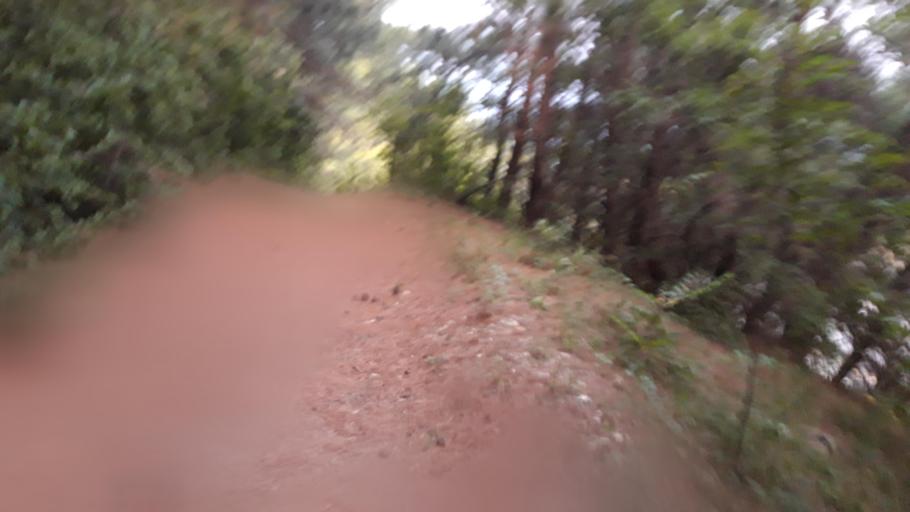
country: RU
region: Krasnodarskiy
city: Gelendzhik
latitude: 44.5797
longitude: 38.0852
